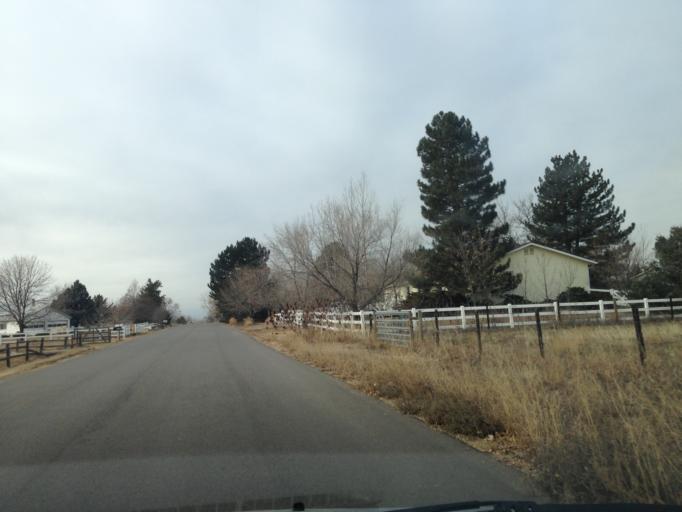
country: US
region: Colorado
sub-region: Boulder County
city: Erie
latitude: 40.0450
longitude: -105.0762
